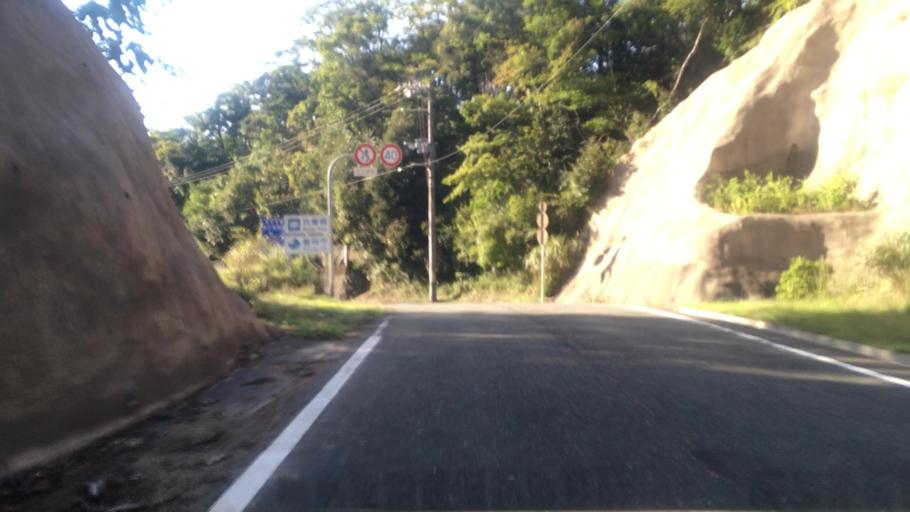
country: JP
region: Hyogo
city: Toyooka
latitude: 35.6190
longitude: 134.8727
